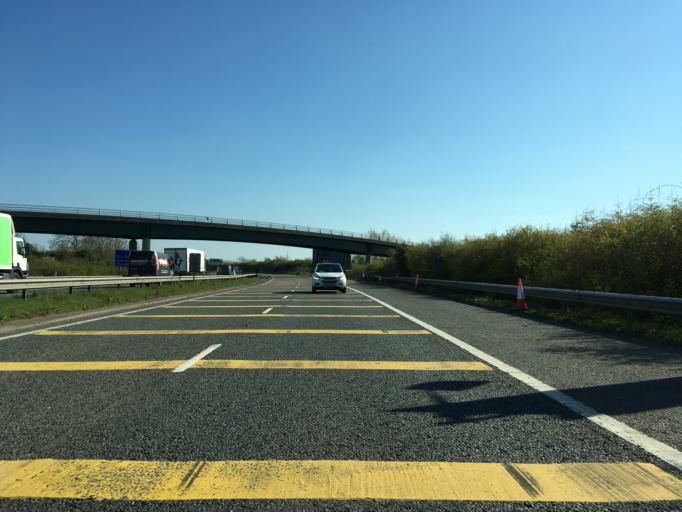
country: GB
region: England
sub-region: South Gloucestershire
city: Severn Beach
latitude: 51.5674
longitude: -2.6590
